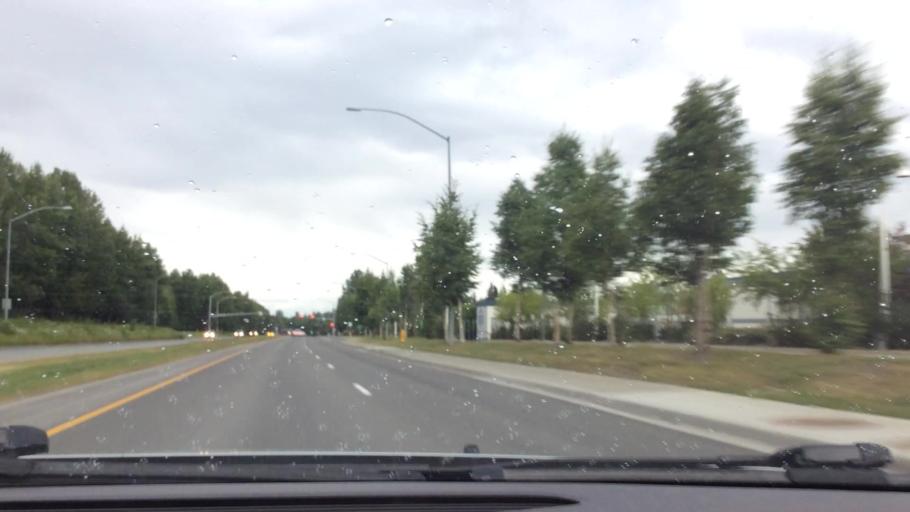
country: US
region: Alaska
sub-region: Anchorage Municipality
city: Anchorage
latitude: 61.1990
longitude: -149.8032
